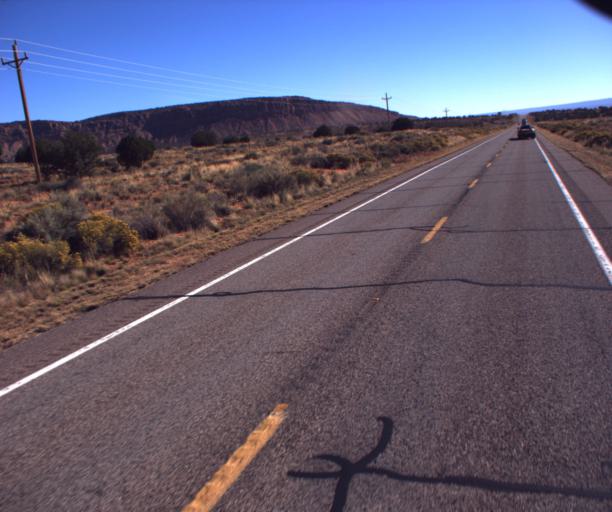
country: US
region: Arizona
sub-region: Mohave County
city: Colorado City
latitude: 36.8582
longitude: -112.7881
